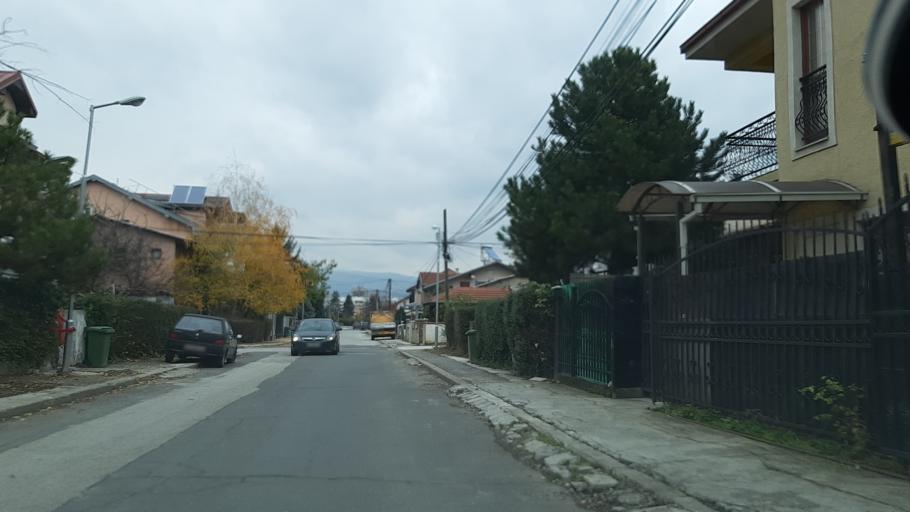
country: MK
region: Kisela Voda
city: Usje
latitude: 41.9752
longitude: 21.4701
